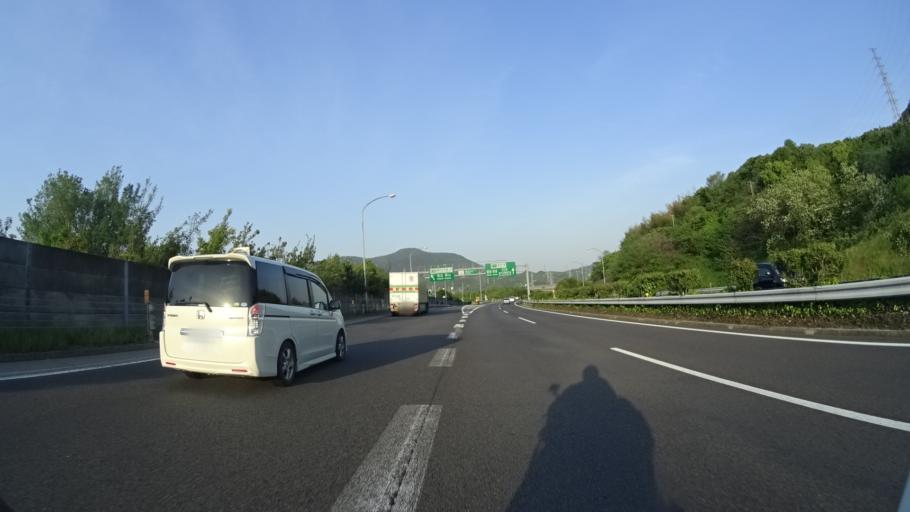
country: JP
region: Kagawa
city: Sakaidecho
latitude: 34.2820
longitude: 133.8460
